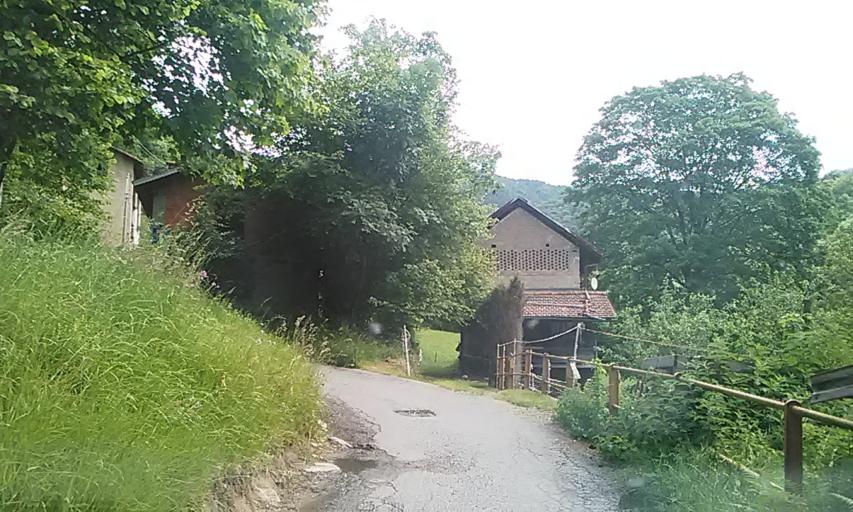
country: IT
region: Piedmont
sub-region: Provincia di Vercelli
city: Civiasco
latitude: 45.8176
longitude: 8.3124
